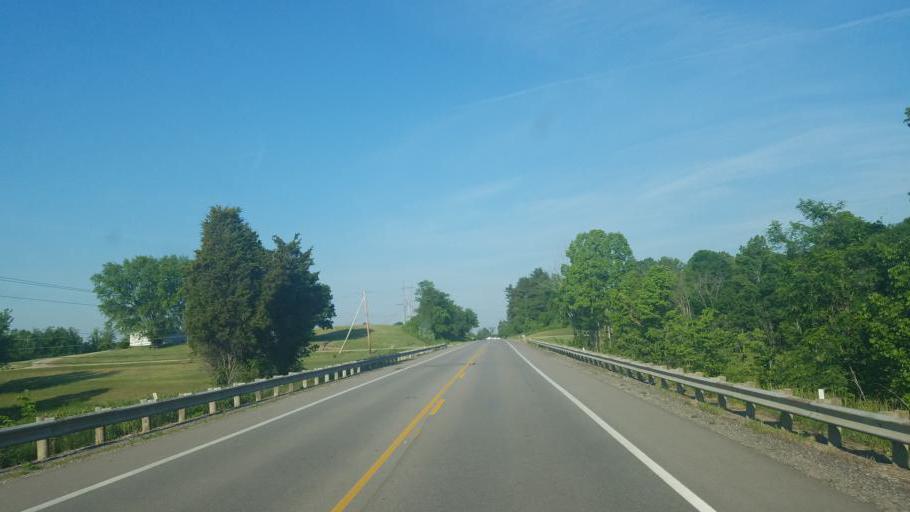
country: US
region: West Virginia
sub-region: Mason County
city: New Haven
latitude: 39.1359
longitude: -81.8620
